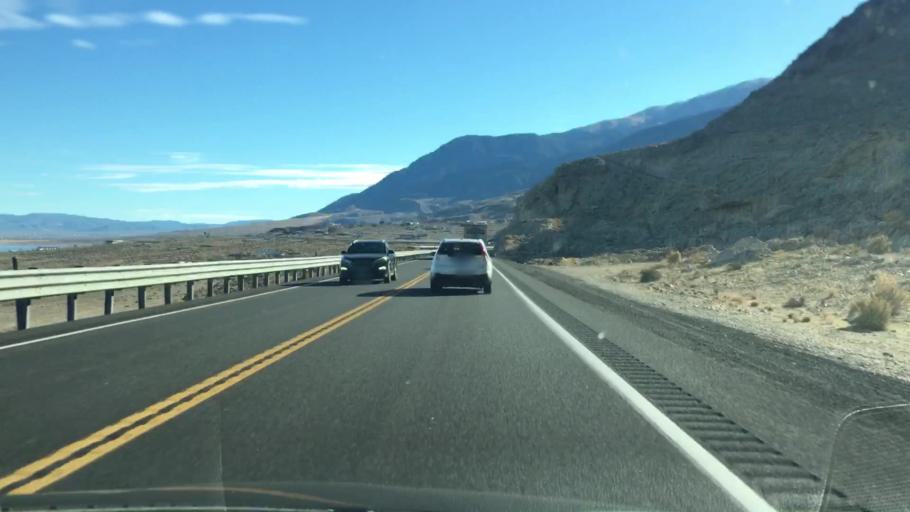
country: US
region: Nevada
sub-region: Mineral County
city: Hawthorne
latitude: 38.6658
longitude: -118.7670
